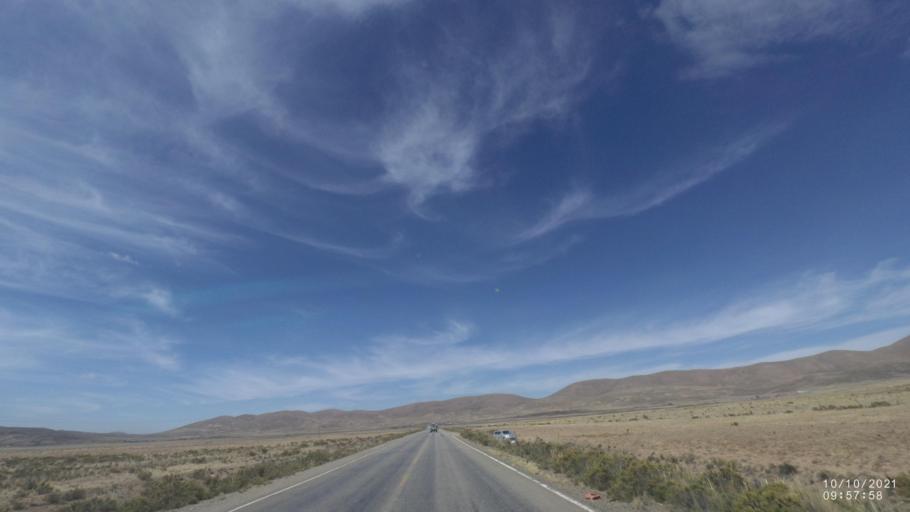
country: BO
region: La Paz
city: Colquiri
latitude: -17.3443
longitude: -67.3906
